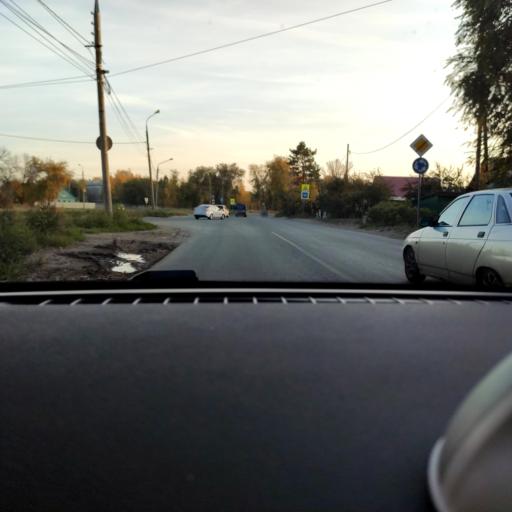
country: RU
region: Samara
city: Smyshlyayevka
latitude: 53.2333
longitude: 50.3070
